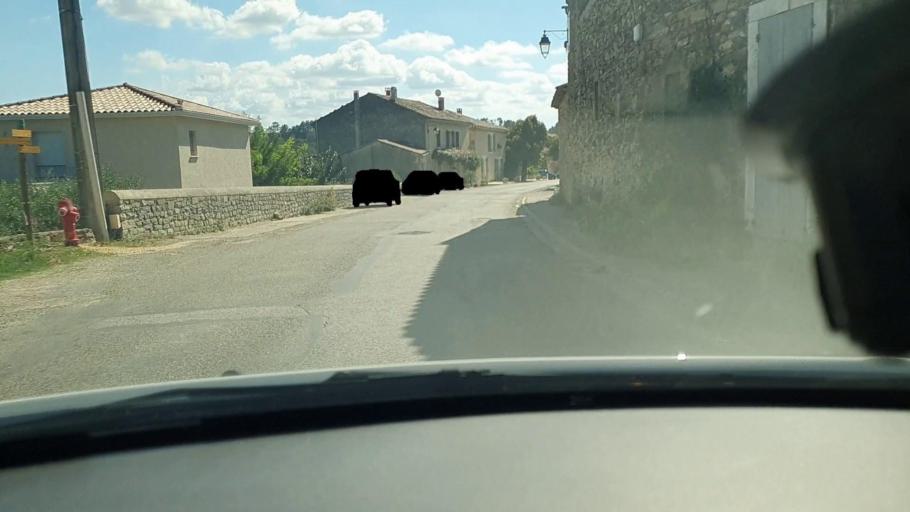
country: FR
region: Languedoc-Roussillon
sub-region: Departement du Gard
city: Goudargues
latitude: 44.1629
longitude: 4.4858
